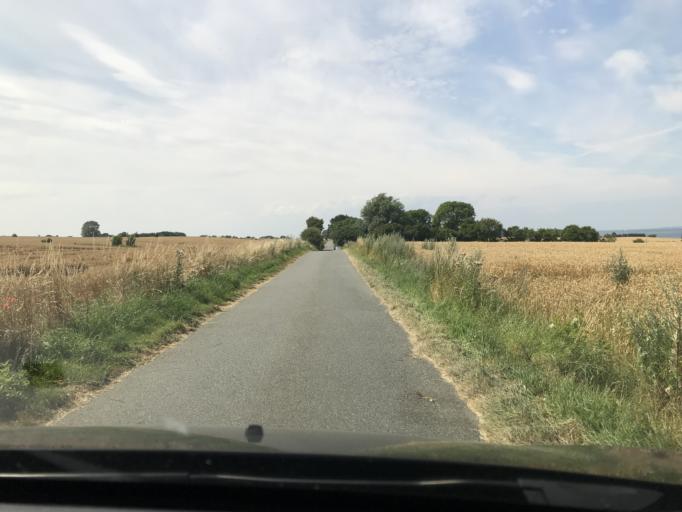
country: DK
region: South Denmark
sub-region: AEro Kommune
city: AEroskobing
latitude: 54.9369
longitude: 10.2757
